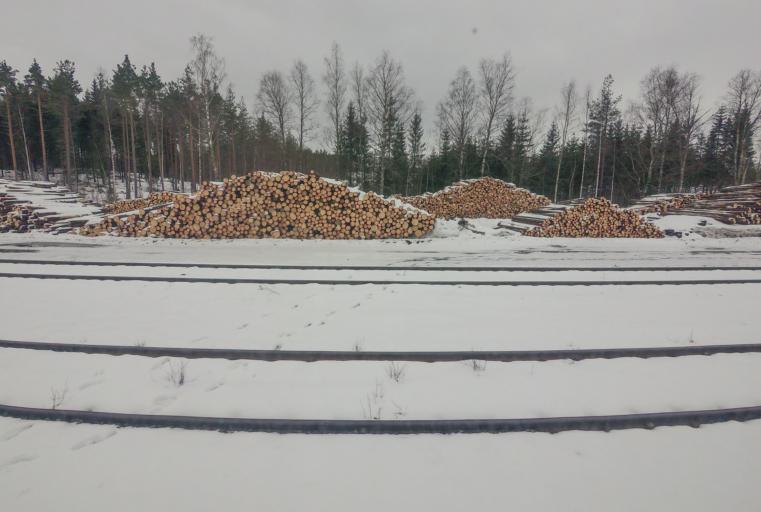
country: FI
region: Southern Savonia
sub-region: Savonlinna
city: Kerimaeki
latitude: 61.8618
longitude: 29.1133
